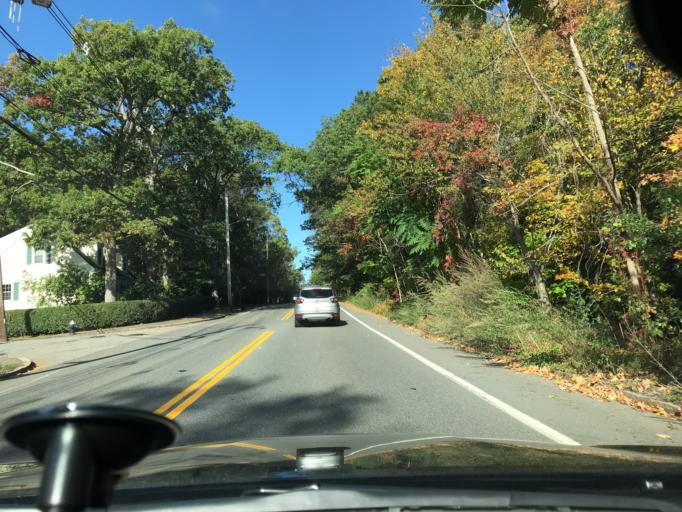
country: US
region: Massachusetts
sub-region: Suffolk County
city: Jamaica Plain
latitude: 42.3028
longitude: -71.1416
